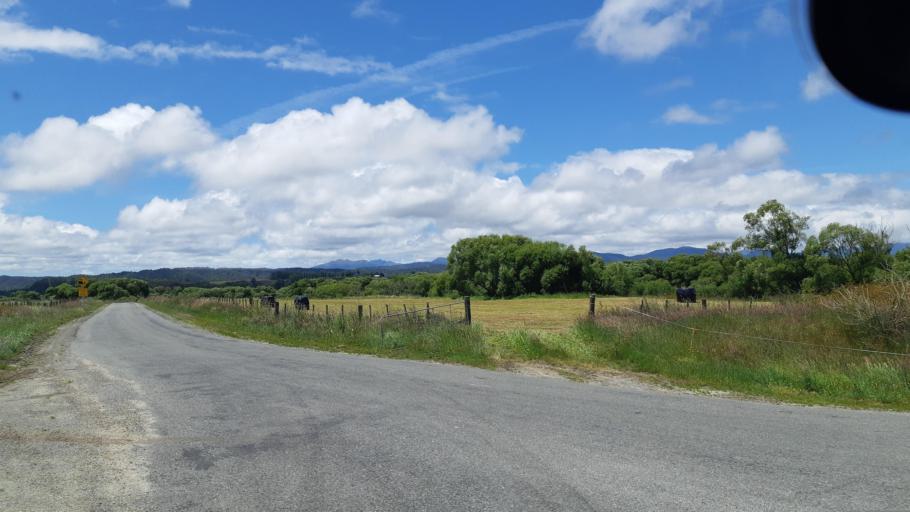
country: NZ
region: West Coast
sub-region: Grey District
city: Greymouth
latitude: -42.2699
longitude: 171.6704
